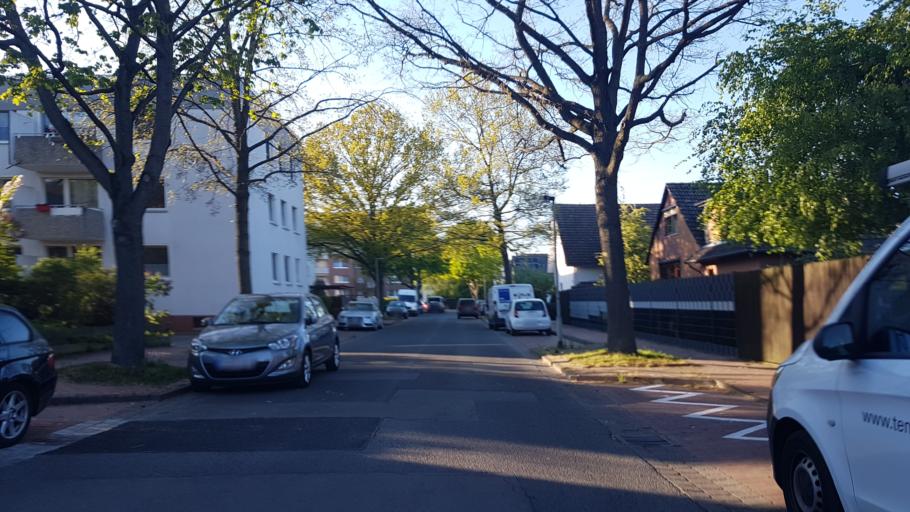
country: DE
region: Lower Saxony
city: Isernhagen Farster Bauerschaft
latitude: 52.3959
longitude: 9.8126
